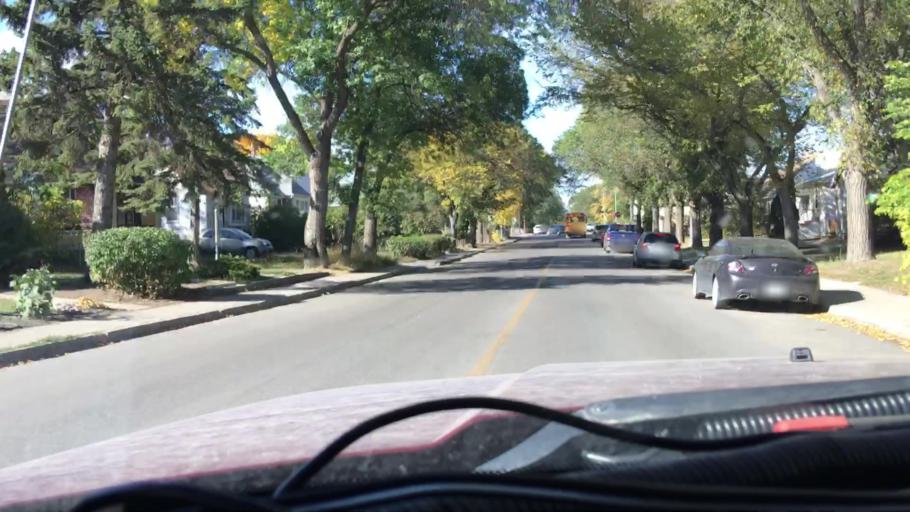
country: CA
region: Saskatchewan
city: Regina
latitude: 50.4602
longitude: -104.6312
